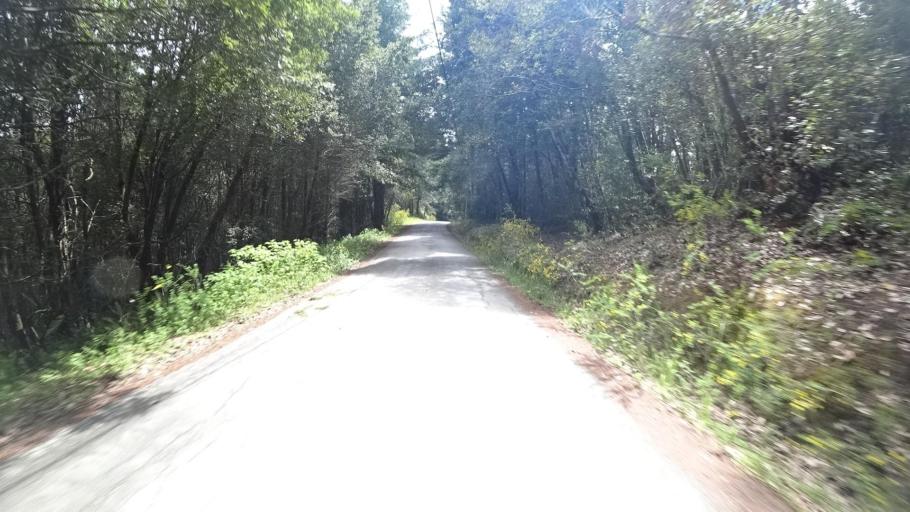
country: US
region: California
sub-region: Humboldt County
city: Blue Lake
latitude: 40.7973
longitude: -123.8756
